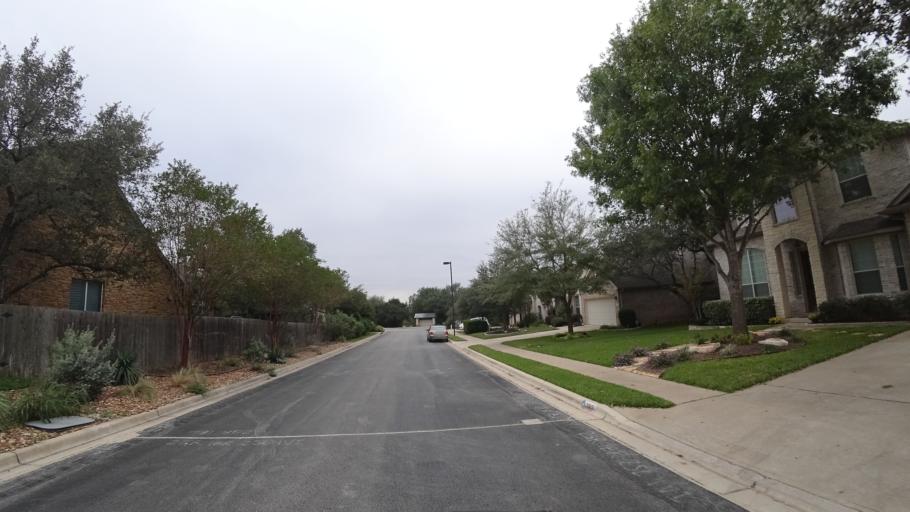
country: US
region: Texas
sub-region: Travis County
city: Shady Hollow
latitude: 30.1888
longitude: -97.9097
